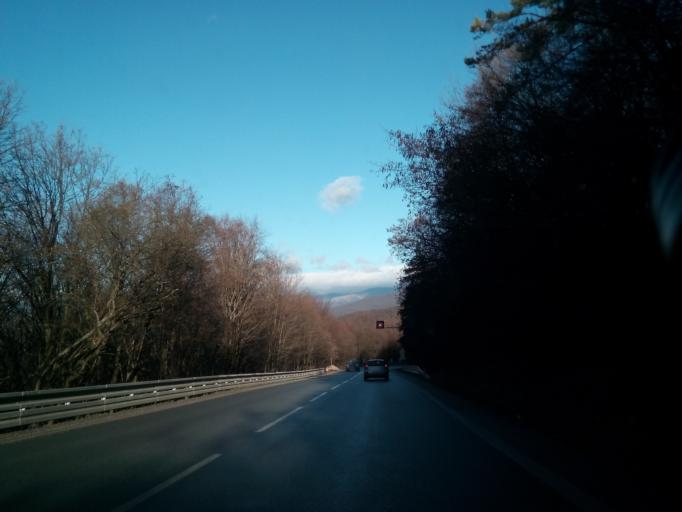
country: SK
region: Kosicky
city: Roznava
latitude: 48.6225
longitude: 20.6316
